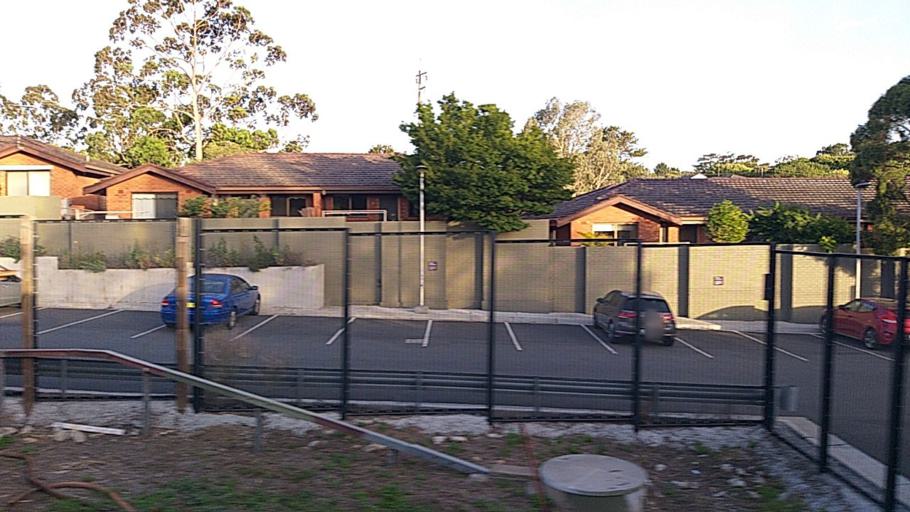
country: AU
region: New South Wales
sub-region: Hurstville
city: Oatley
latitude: -33.9819
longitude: 151.0788
